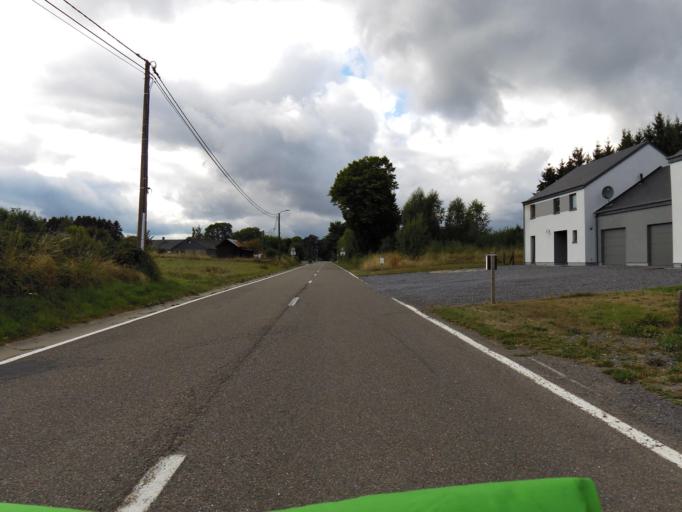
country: BE
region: Wallonia
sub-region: Province de Namur
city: Bievre
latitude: 49.9365
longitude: 5.0292
